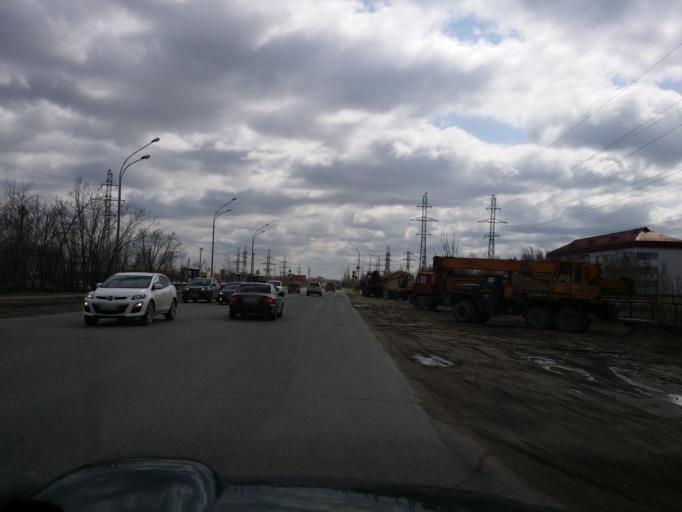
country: RU
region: Khanty-Mansiyskiy Avtonomnyy Okrug
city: Nizhnevartovsk
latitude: 60.9370
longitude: 76.5306
